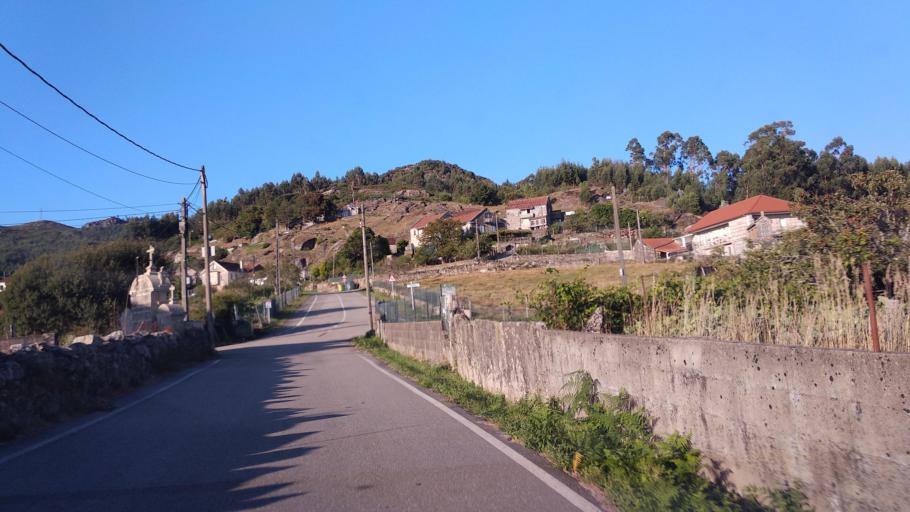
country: ES
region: Galicia
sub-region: Provincia de Pontevedra
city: Ponte Caldelas
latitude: 42.3577
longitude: -8.4906
